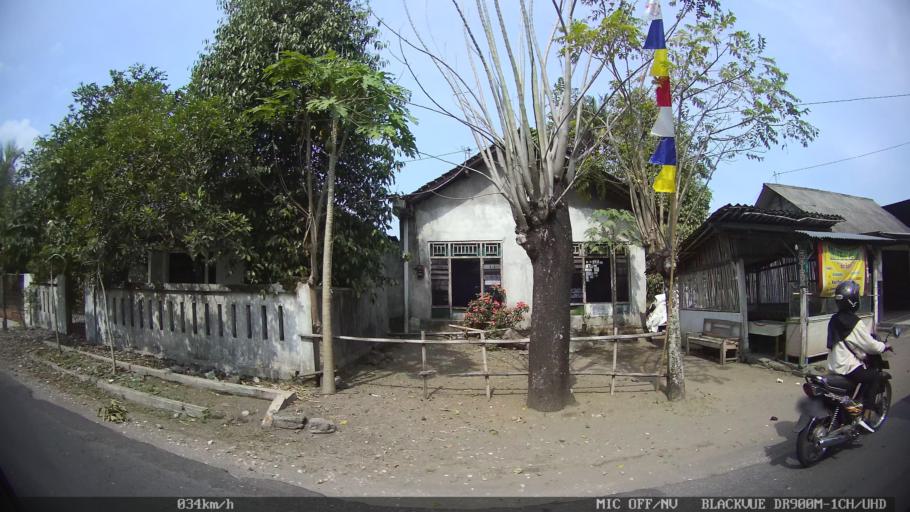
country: ID
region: Daerah Istimewa Yogyakarta
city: Depok
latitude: -7.7898
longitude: 110.4471
